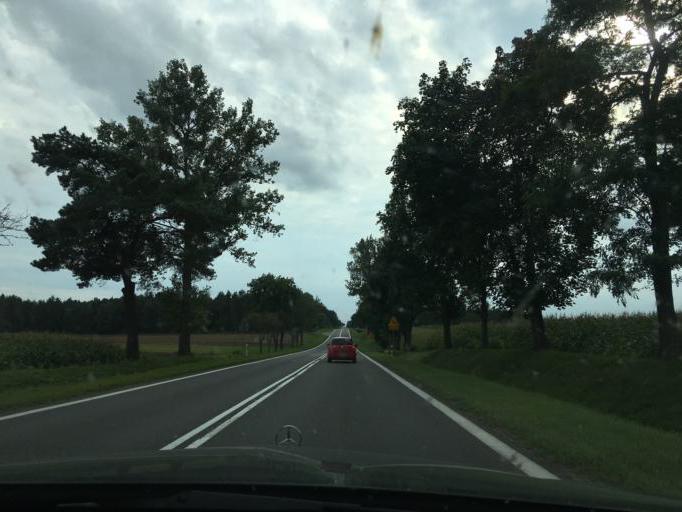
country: PL
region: Podlasie
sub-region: Powiat kolnenski
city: Stawiski
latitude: 53.4499
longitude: 22.1862
